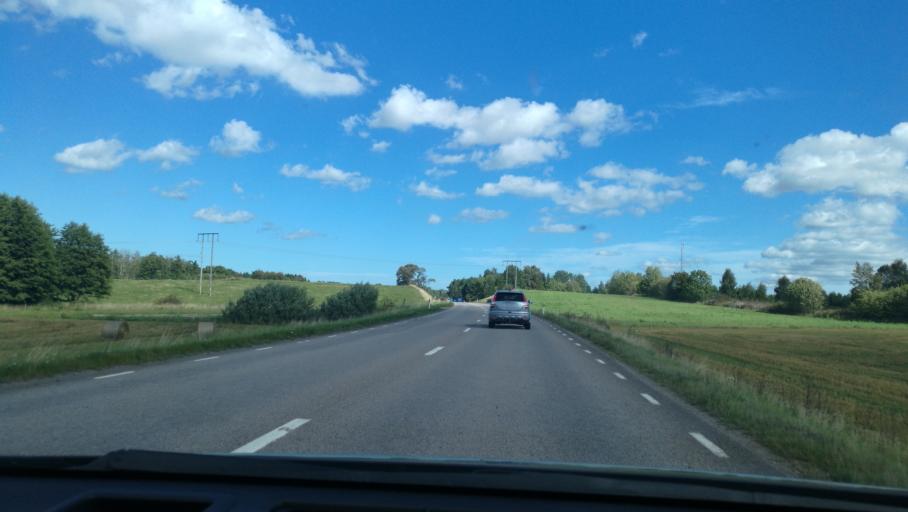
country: SE
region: Vaestra Goetaland
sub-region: Gotene Kommun
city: Kallby
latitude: 58.4936
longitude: 13.2945
